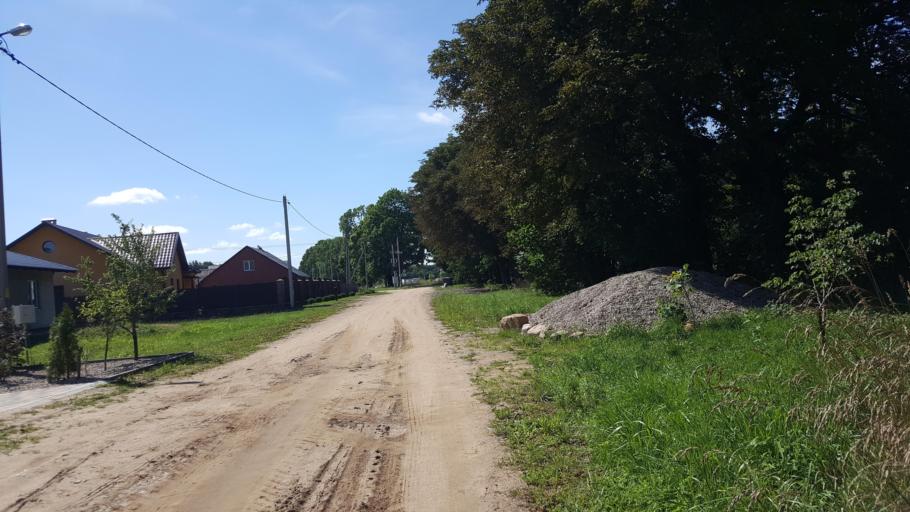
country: BY
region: Brest
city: Charnawchytsy
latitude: 52.2697
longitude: 23.7634
